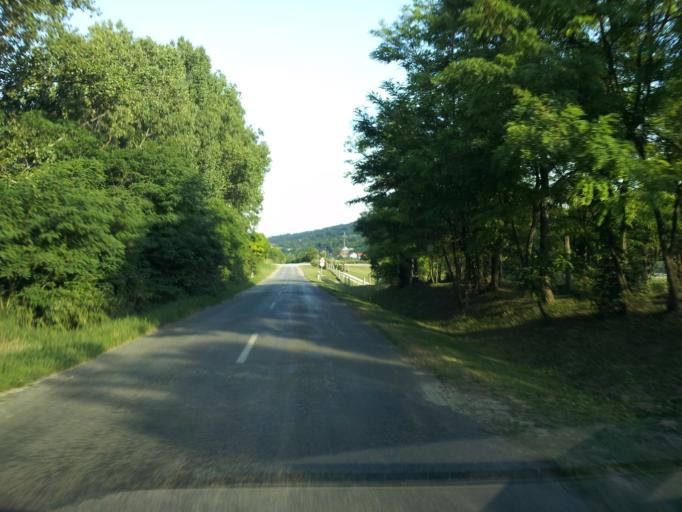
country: HU
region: Fejer
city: Many
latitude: 47.5303
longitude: 18.5965
